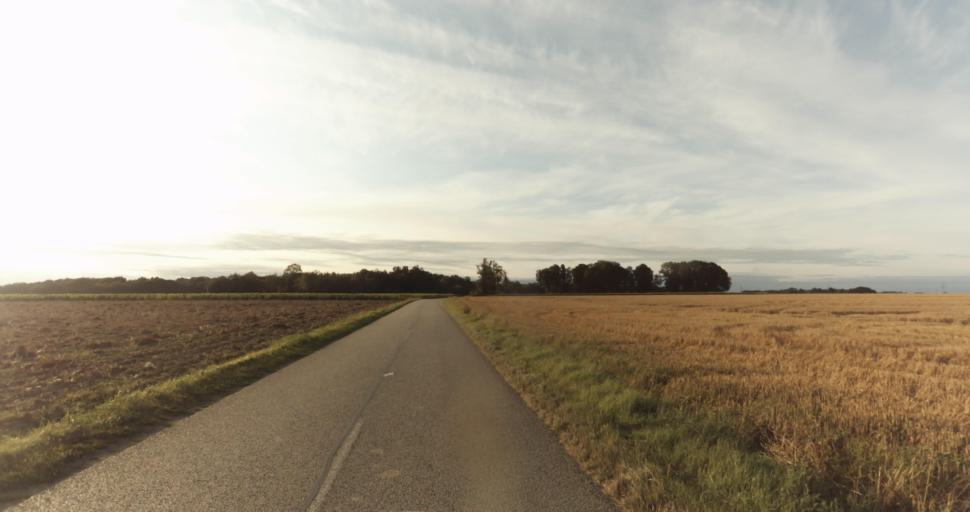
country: FR
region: Haute-Normandie
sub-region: Departement de l'Eure
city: Saint-Germain-sur-Avre
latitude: 48.8282
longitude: 1.2615
